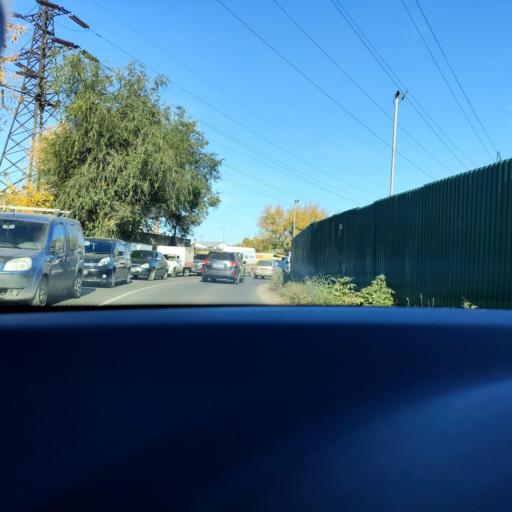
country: RU
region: Samara
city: Petra-Dubrava
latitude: 53.2517
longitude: 50.2947
